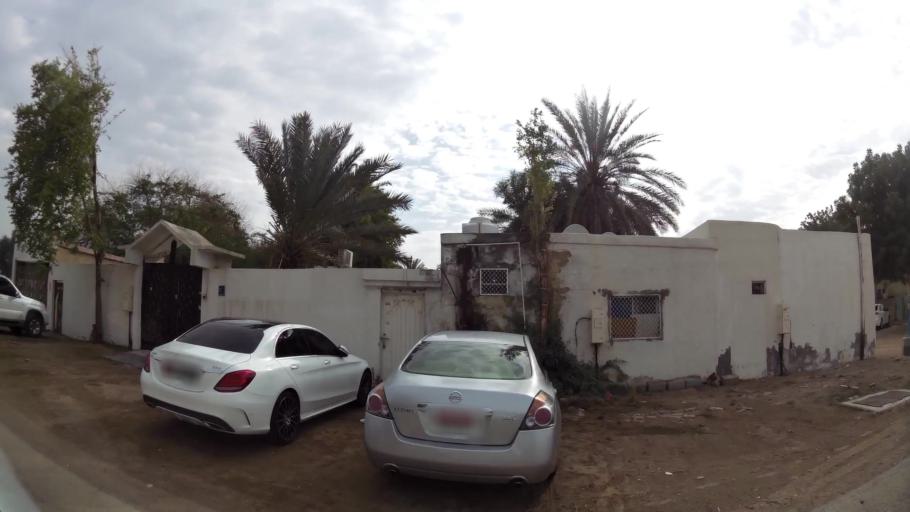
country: AE
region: Abu Dhabi
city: Al Ain
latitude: 24.2239
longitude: 55.7408
